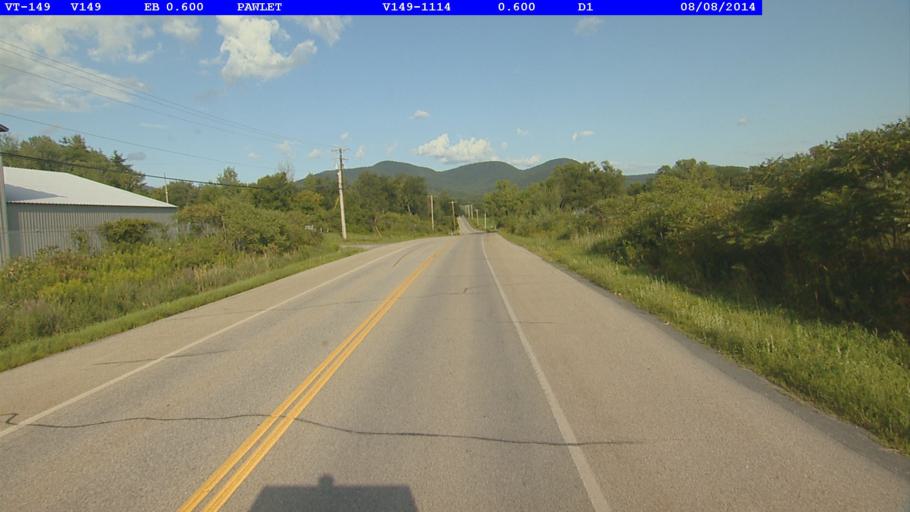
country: US
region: New York
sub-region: Washington County
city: Granville
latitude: 43.4034
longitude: -73.2398
